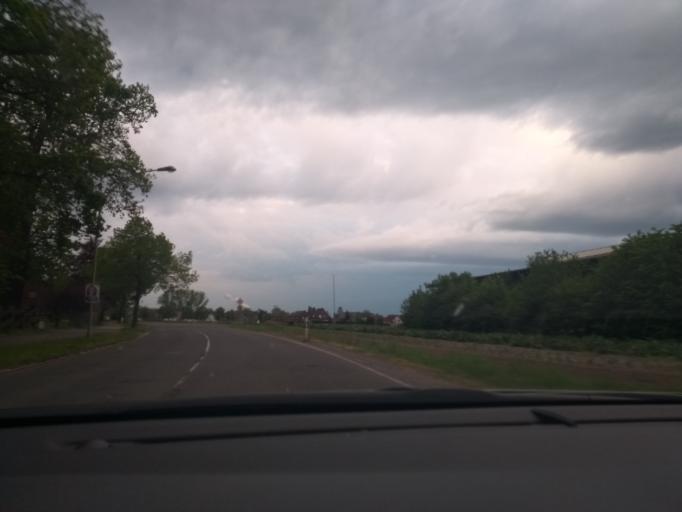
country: DE
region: North Rhine-Westphalia
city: Selm
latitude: 51.6561
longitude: 7.4632
